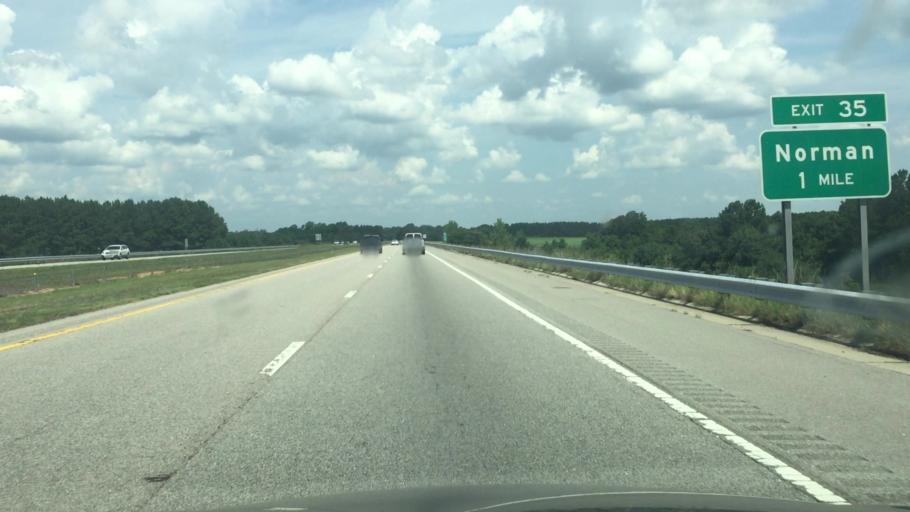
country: US
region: North Carolina
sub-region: Richmond County
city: Ellerbe
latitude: 35.1543
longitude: -79.7152
